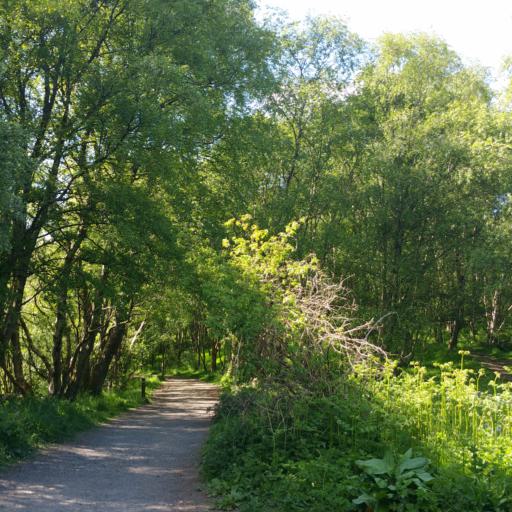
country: GB
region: Scotland
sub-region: East Dunbartonshire
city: Milngavie
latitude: 55.9552
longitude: -4.3276
